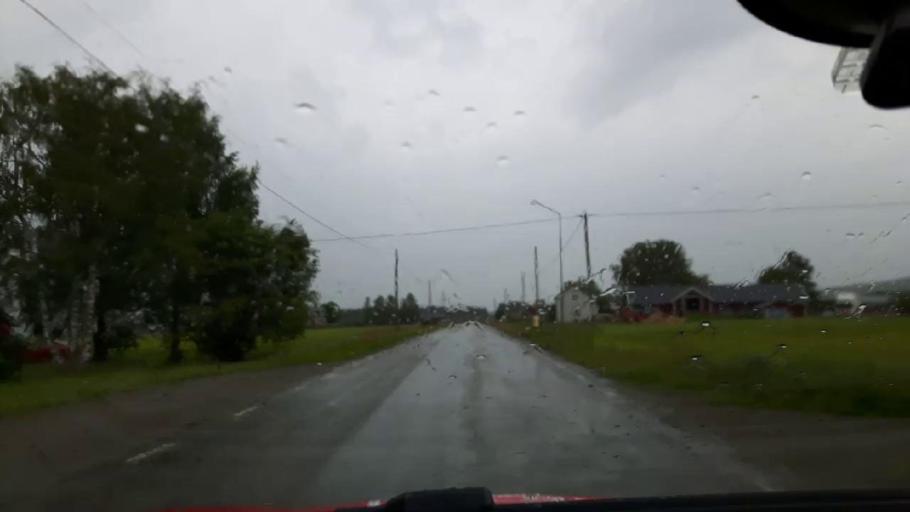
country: SE
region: Jaemtland
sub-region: OEstersunds Kommun
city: Brunflo
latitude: 62.9872
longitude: 14.8096
